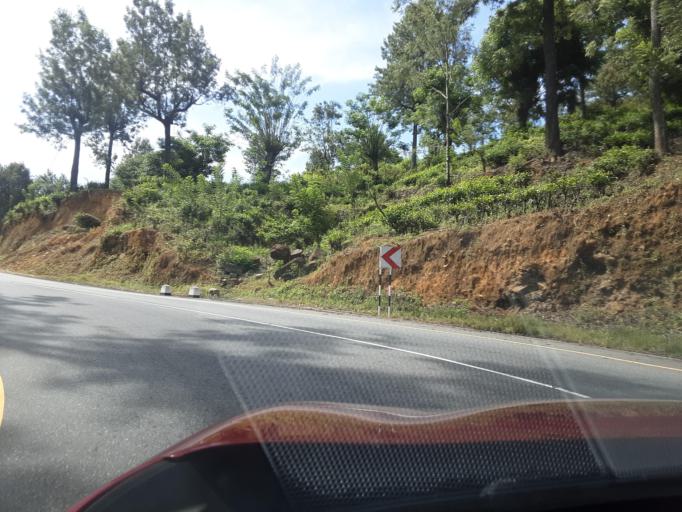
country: LK
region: Uva
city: Badulla
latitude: 6.9591
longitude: 81.1160
